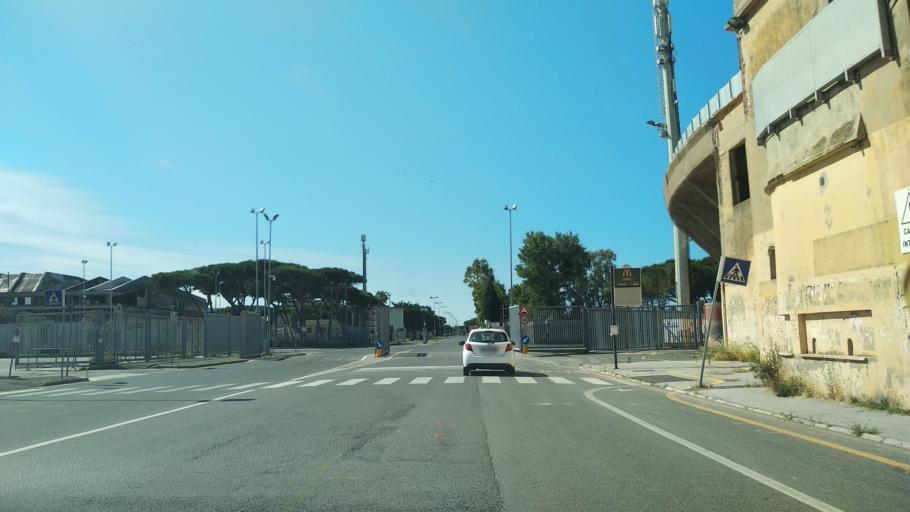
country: IT
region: Tuscany
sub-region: Provincia di Livorno
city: Livorno
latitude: 43.5268
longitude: 10.3155
